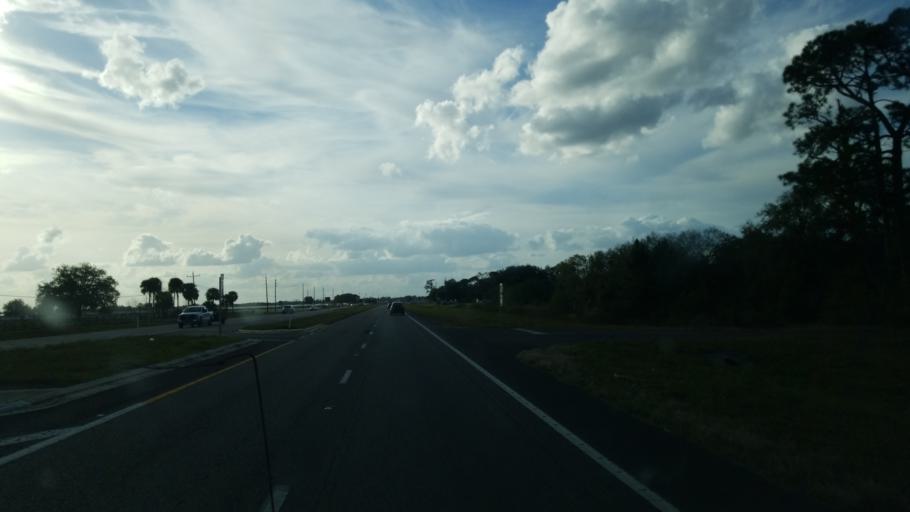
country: US
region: Florida
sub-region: Osceola County
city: Saint Cloud
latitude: 28.2420
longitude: -81.2073
